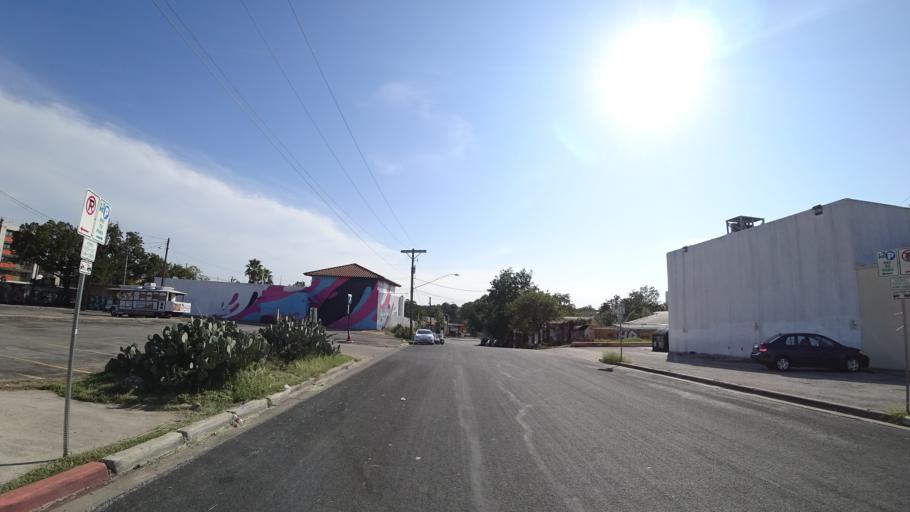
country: US
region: Texas
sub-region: Travis County
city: Austin
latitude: 30.2633
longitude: -97.7276
